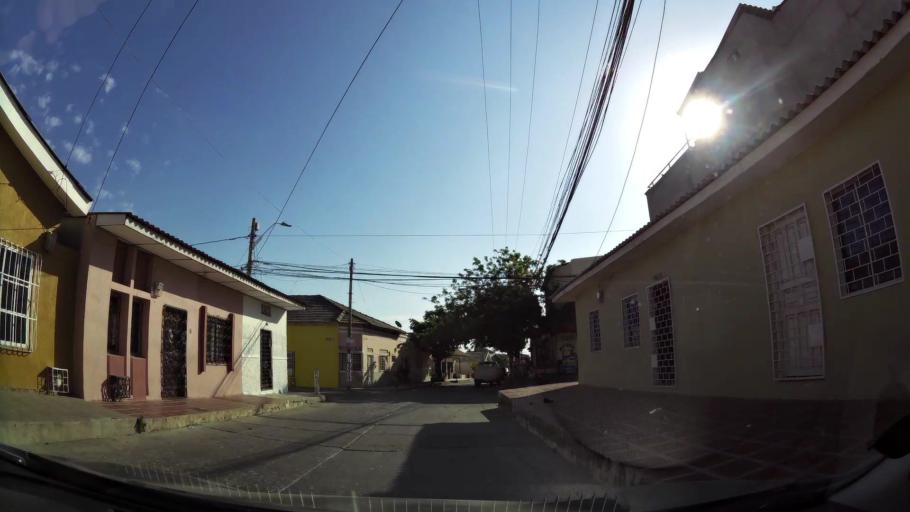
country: CO
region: Atlantico
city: Barranquilla
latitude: 10.9917
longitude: -74.7875
